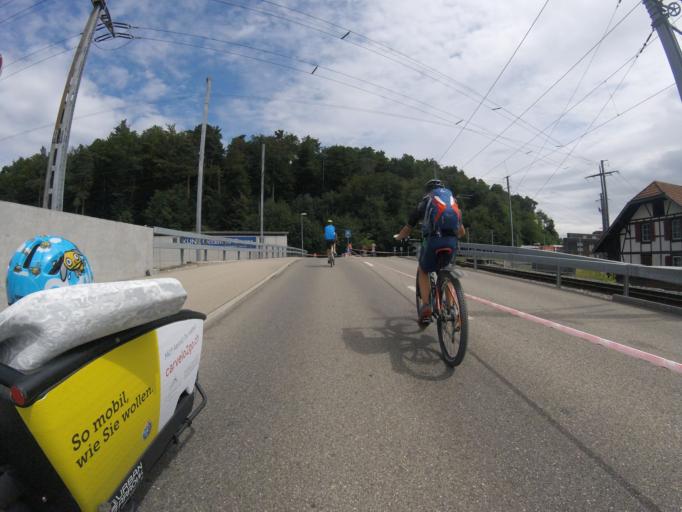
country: CH
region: Bern
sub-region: Bern-Mittelland District
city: Muri
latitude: 46.9364
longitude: 7.5009
